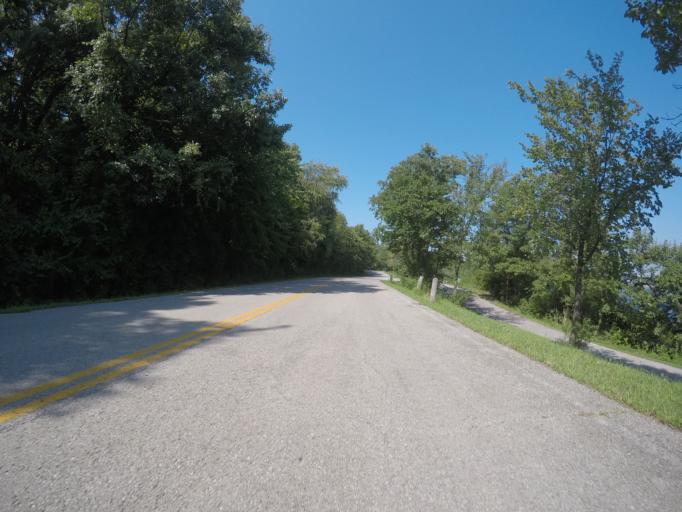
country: US
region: Missouri
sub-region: Platte County
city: Parkville
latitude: 39.1670
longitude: -94.7832
